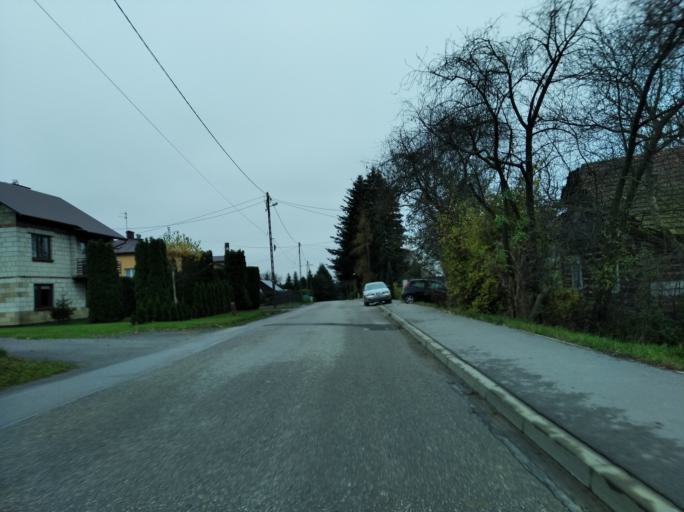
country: PL
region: Subcarpathian Voivodeship
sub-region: Powiat krosnienski
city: Odrzykon
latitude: 49.7308
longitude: 21.7677
